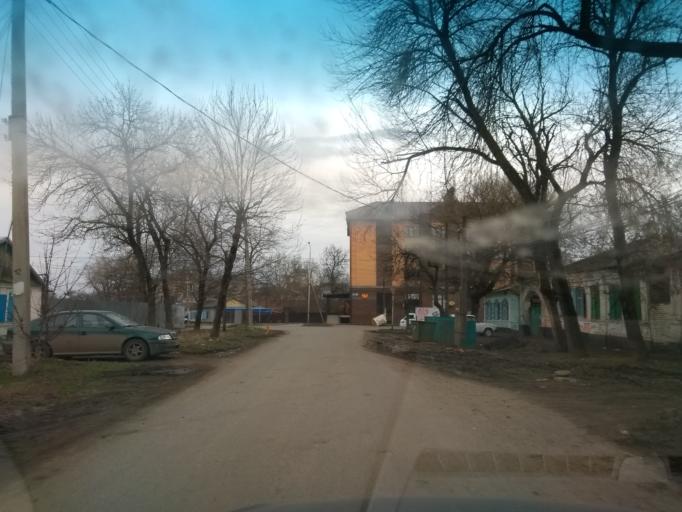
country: RU
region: Stavropol'skiy
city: Georgiyevsk
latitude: 44.1489
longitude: 43.4681
